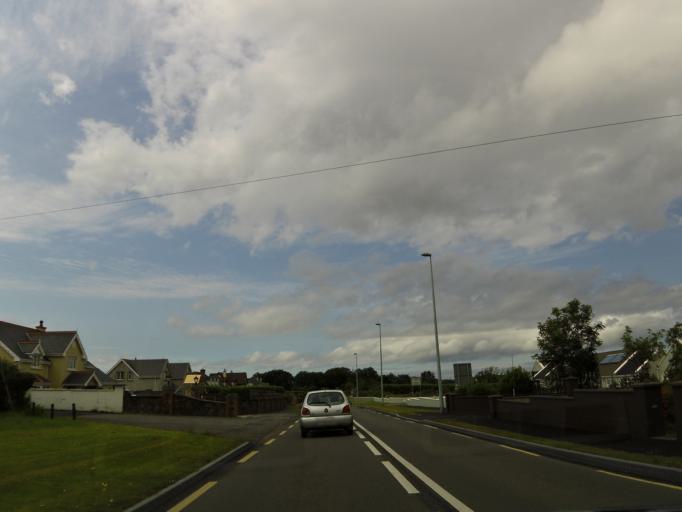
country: IE
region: Munster
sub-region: An Clar
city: Kilrush
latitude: 52.6453
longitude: -9.4944
